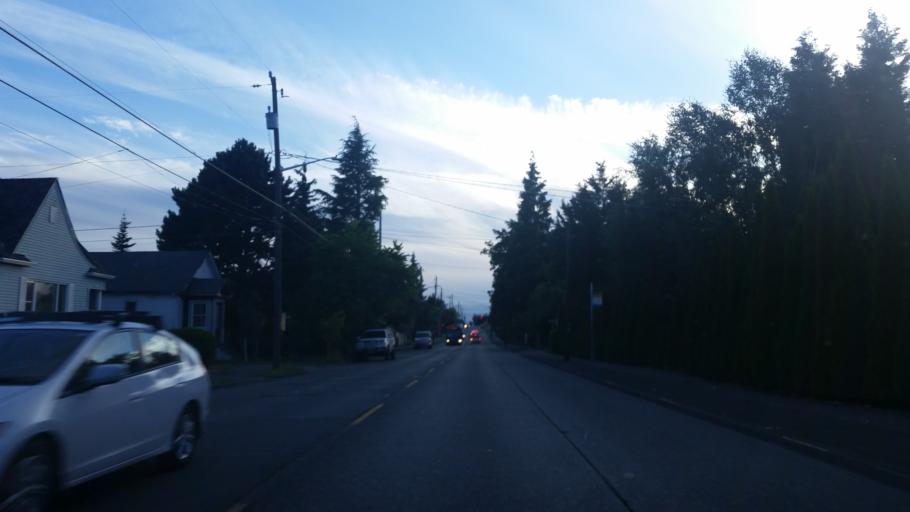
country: US
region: Washington
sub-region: King County
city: Shoreline
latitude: 47.6906
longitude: -122.3842
